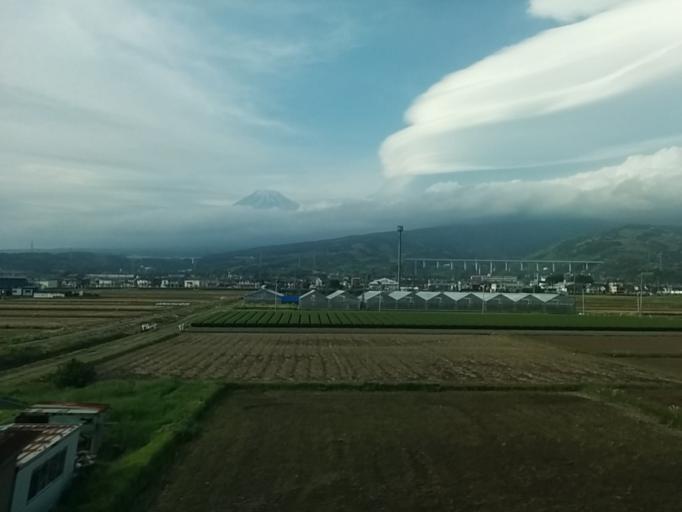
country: JP
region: Shizuoka
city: Fuji
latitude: 35.1541
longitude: 138.7333
